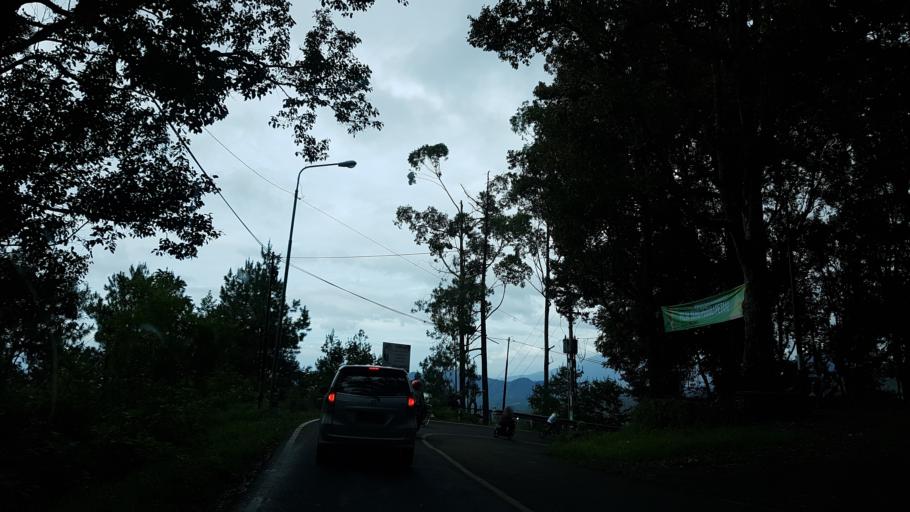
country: ID
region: West Java
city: Banjar
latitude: -7.1326
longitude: 107.4124
